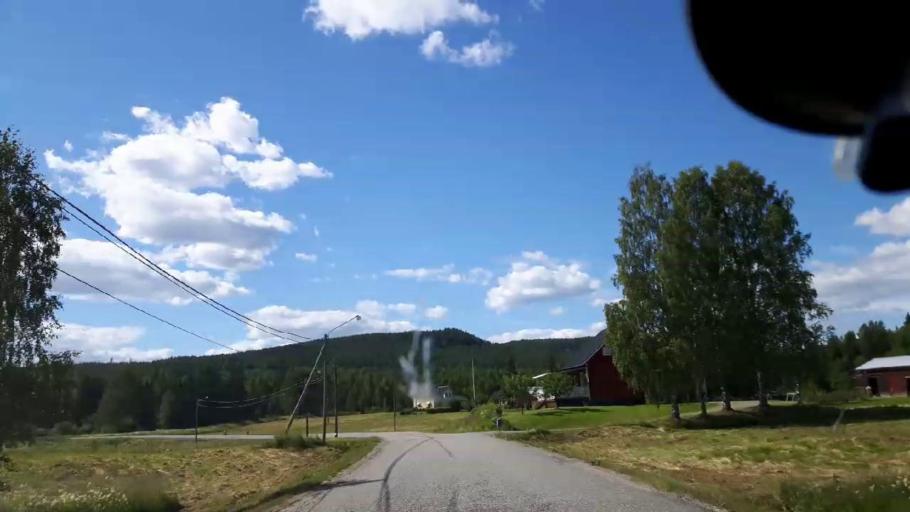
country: SE
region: Vaesternorrland
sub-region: Ange Kommun
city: Fransta
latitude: 62.7823
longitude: 15.9999
